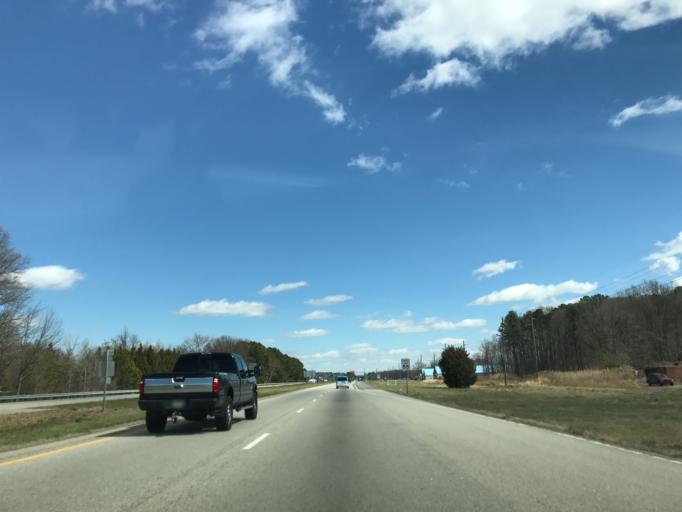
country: US
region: Maryland
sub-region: Queen Anne's County
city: Grasonville
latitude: 38.9853
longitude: -76.1596
